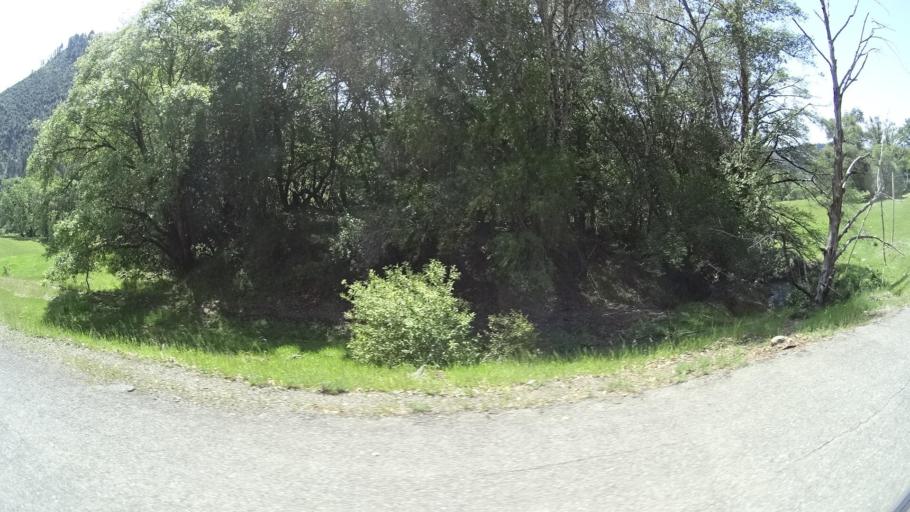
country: US
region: California
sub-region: Humboldt County
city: Redway
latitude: 40.2318
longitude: -123.6167
